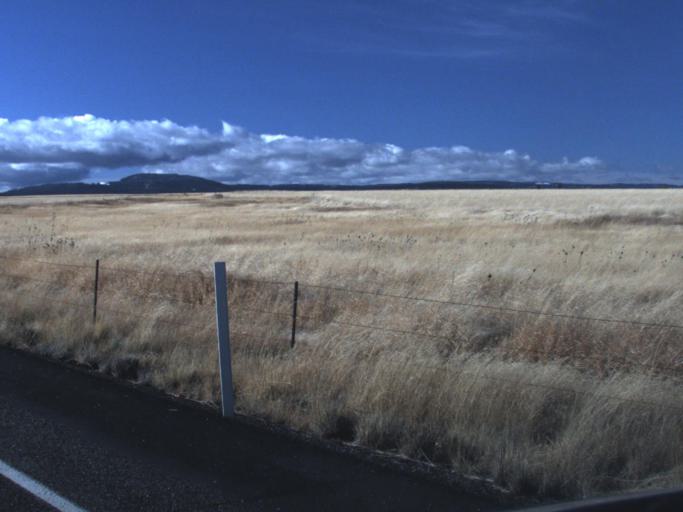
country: US
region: Washington
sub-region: Asotin County
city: Asotin
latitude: 46.1522
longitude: -117.1168
